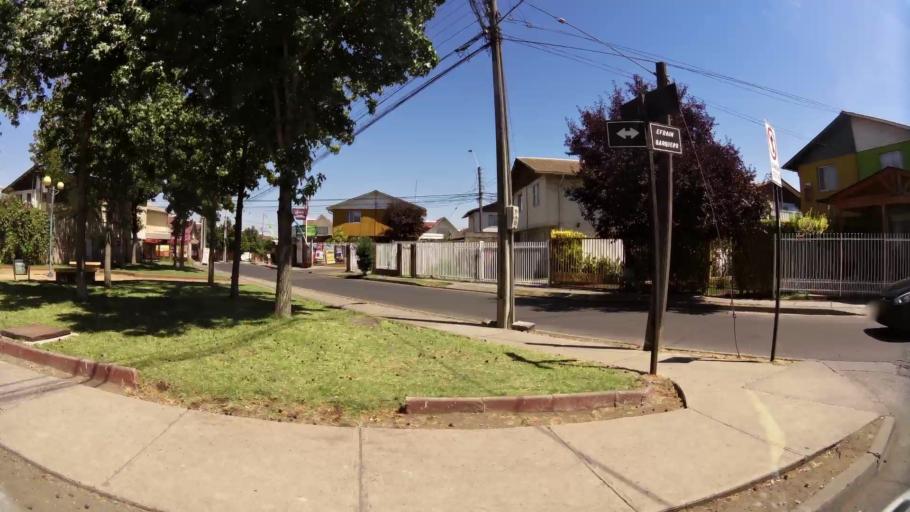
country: CL
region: Maule
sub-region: Provincia de Curico
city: Curico
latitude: -34.9684
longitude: -71.2218
